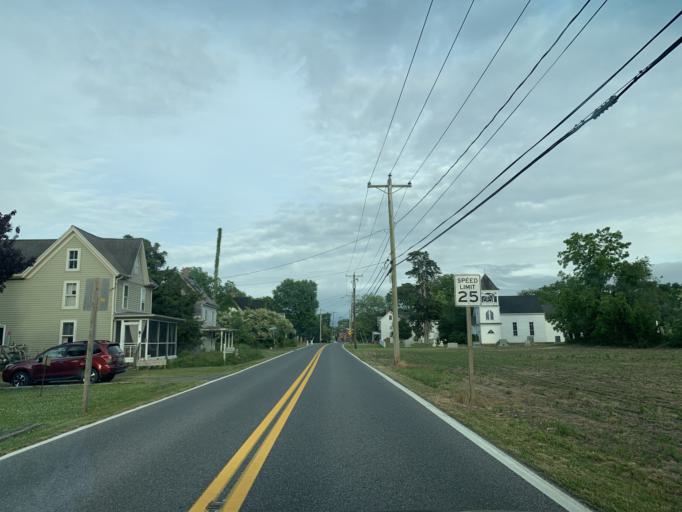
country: US
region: Virginia
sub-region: Accomack County
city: Captains Cove
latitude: 38.0554
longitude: -75.4138
